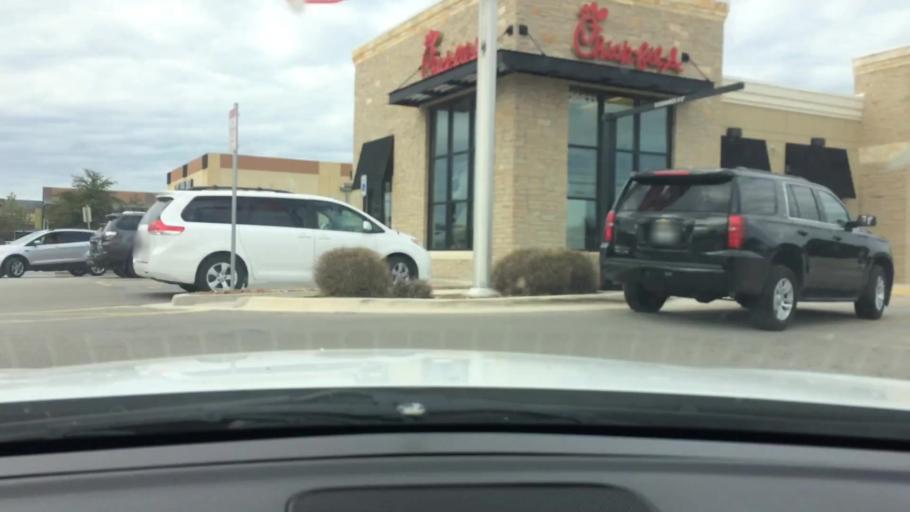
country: US
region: Texas
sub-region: Bexar County
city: Hollywood Park
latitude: 29.6384
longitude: -98.4565
